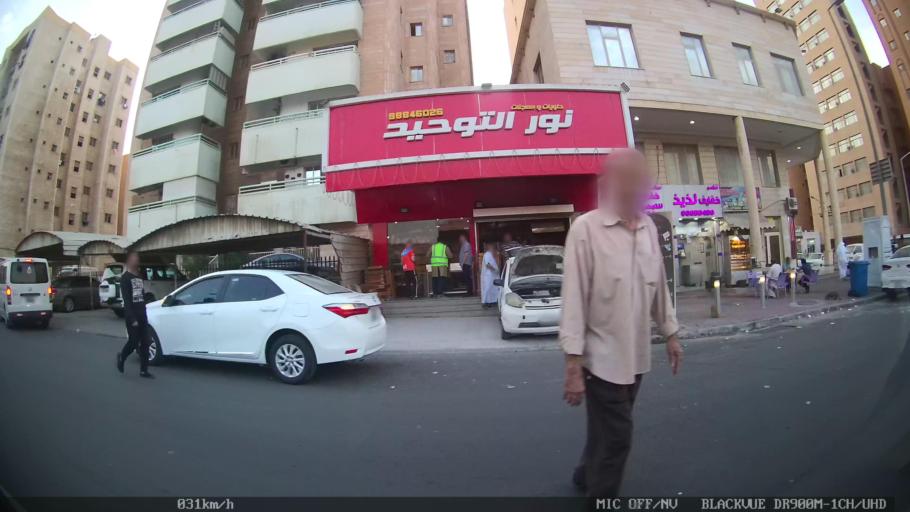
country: KW
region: Al Farwaniyah
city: Al Farwaniyah
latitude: 29.2950
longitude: 47.9742
